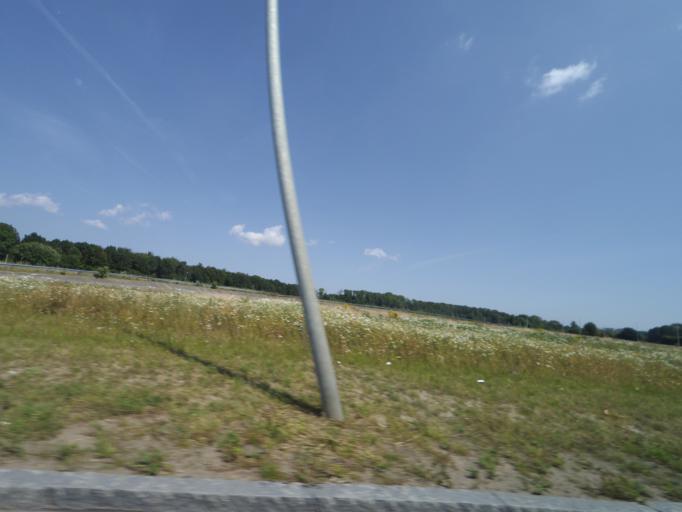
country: DK
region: South Denmark
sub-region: Odense Kommune
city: Hojby
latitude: 55.3549
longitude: 10.4212
